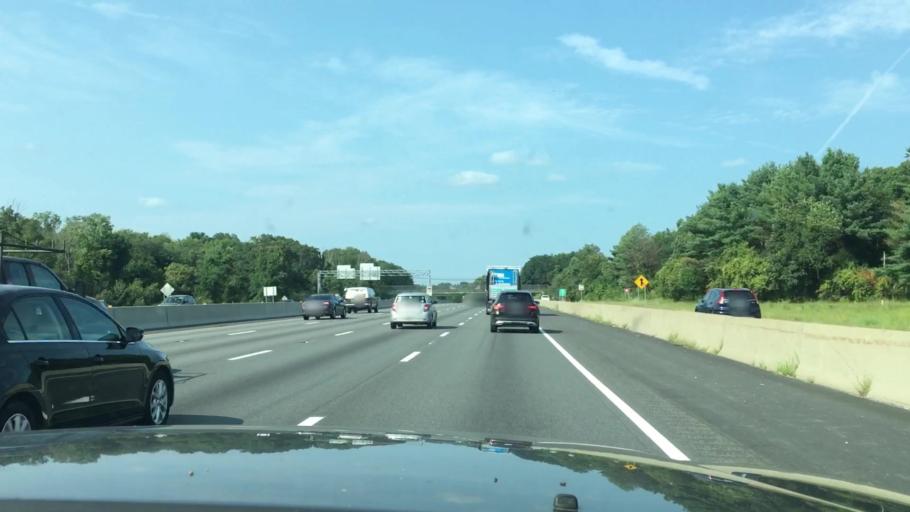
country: US
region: Massachusetts
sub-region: Middlesex County
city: Lexington
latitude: 42.4432
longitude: -71.2567
